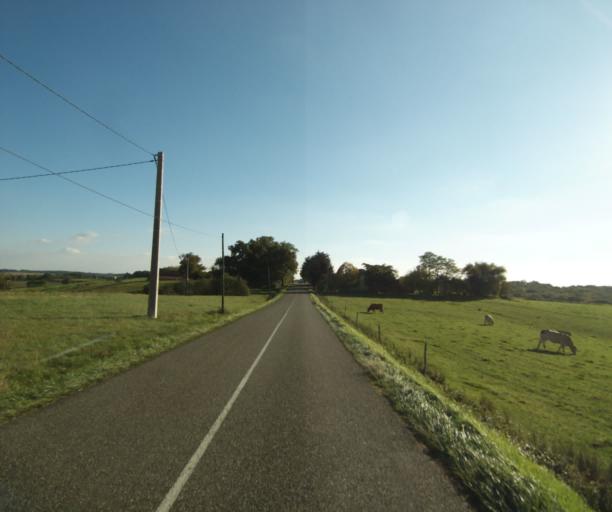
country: FR
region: Midi-Pyrenees
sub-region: Departement du Gers
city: Eauze
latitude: 43.7681
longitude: 0.1290
